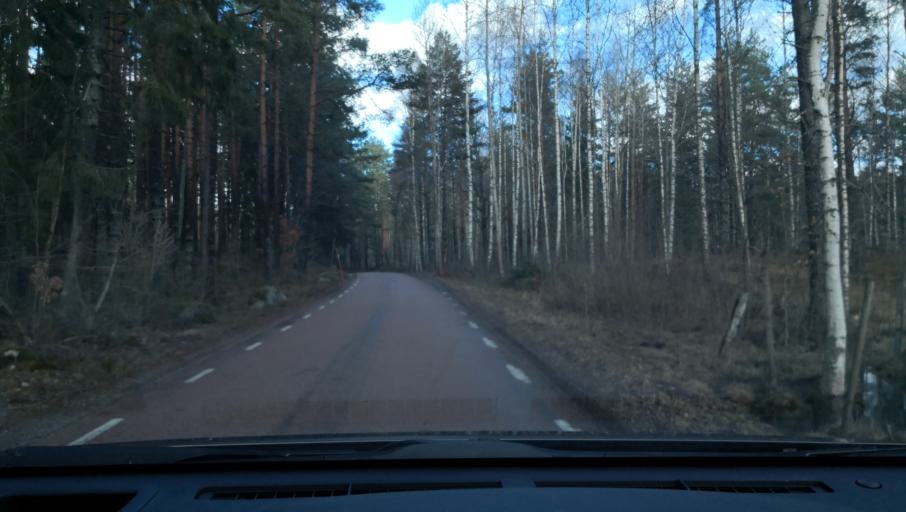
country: SE
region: Vaestmanland
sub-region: Arboga Kommun
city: Arboga
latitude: 59.3190
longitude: 15.7739
